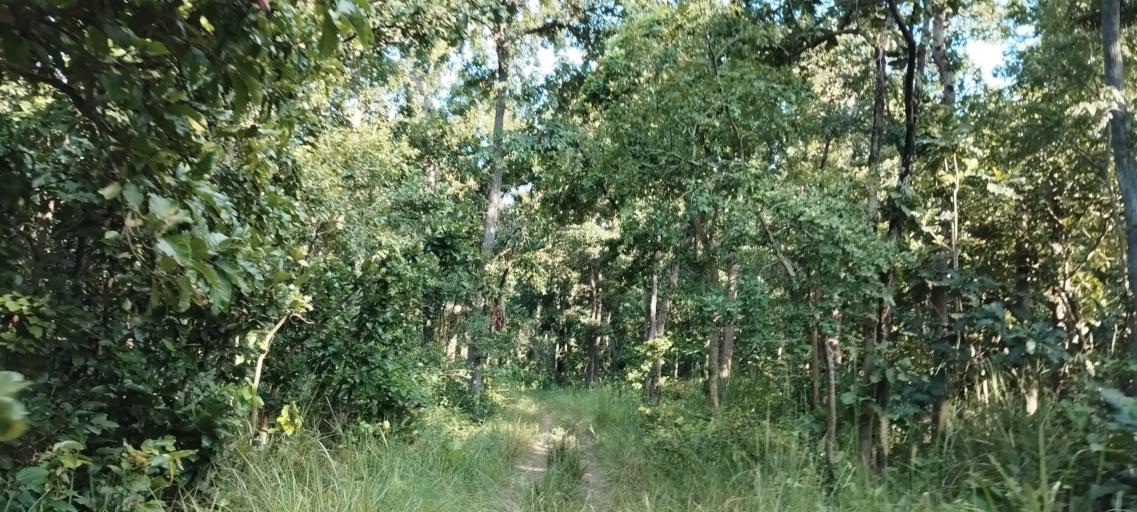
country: NP
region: Far Western
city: Tikapur
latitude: 28.5215
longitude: 81.2722
